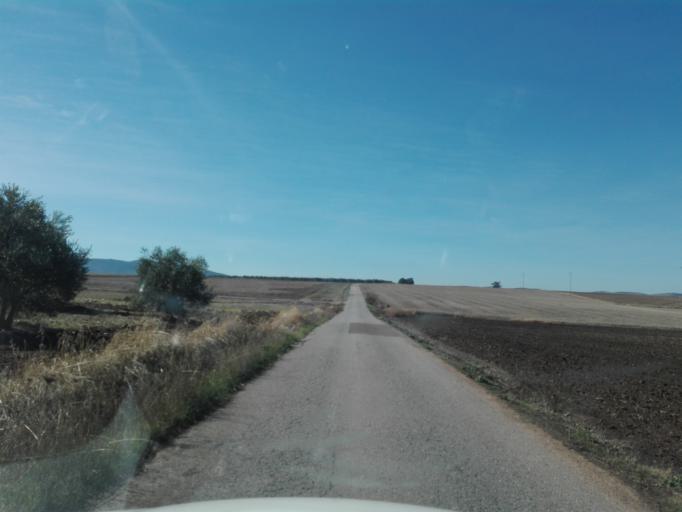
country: ES
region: Extremadura
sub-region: Provincia de Badajoz
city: Llerena
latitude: 38.2822
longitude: -5.9629
